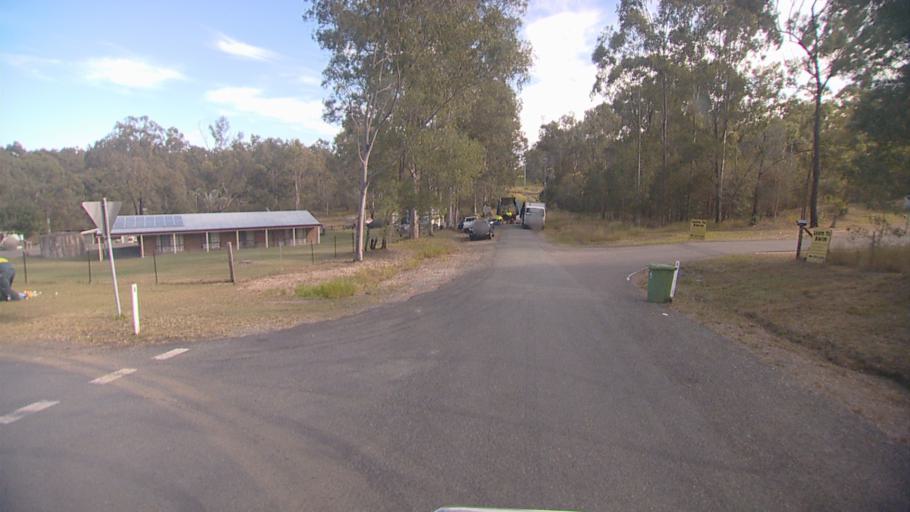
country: AU
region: Queensland
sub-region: Logan
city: North Maclean
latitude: -27.7380
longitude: 152.9791
